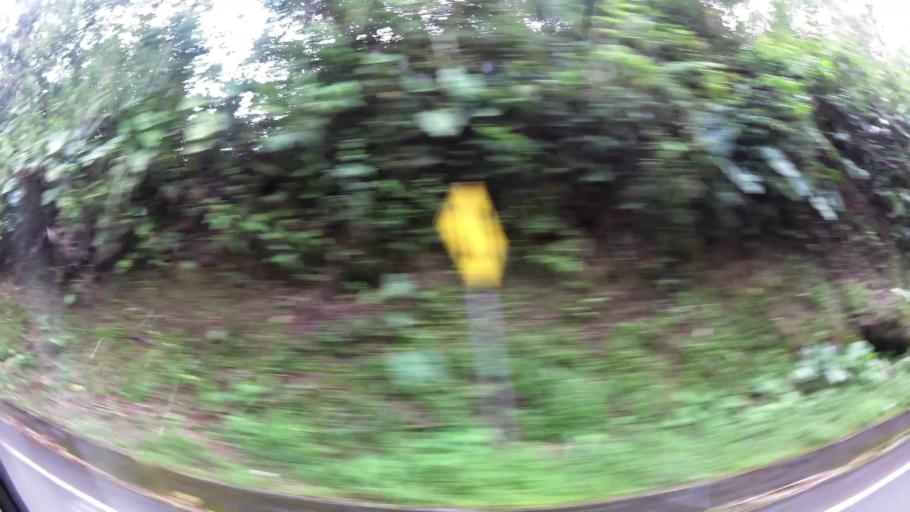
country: EC
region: Pastaza
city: Puyo
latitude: -1.4297
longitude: -78.1771
